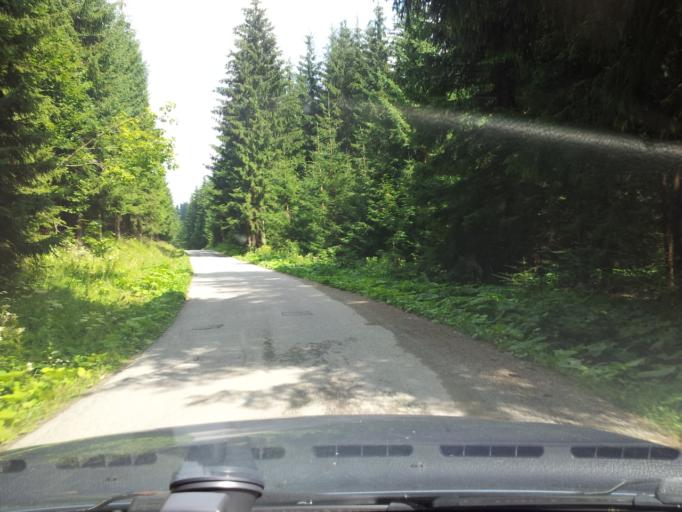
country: SK
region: Zilinsky
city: Oravska Lesna
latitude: 49.3860
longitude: 19.1816
